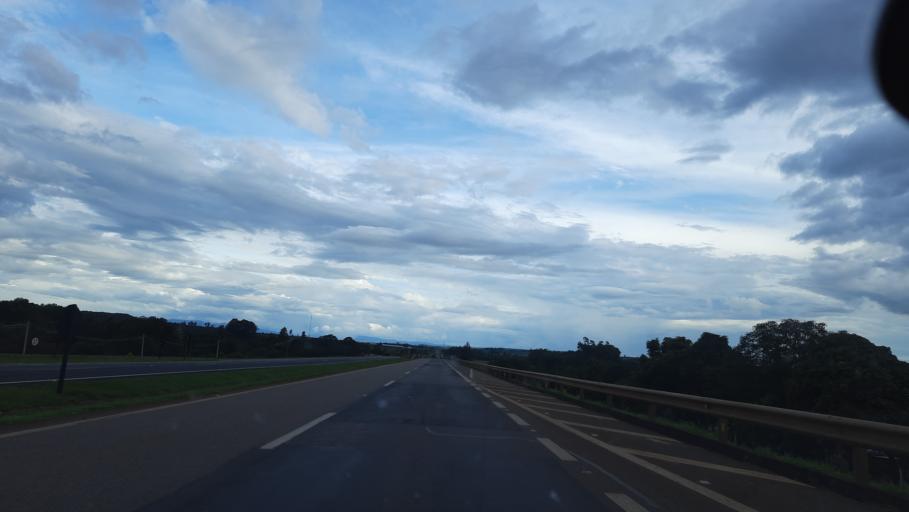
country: BR
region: Sao Paulo
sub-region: Casa Branca
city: Casa Branca
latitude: -21.7704
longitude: -47.0659
